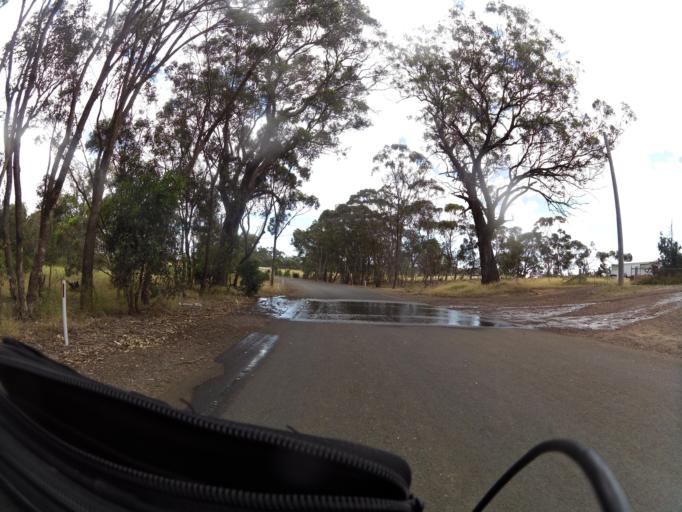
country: AU
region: Victoria
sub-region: Campaspe
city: Kyabram
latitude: -36.7323
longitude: 145.1482
